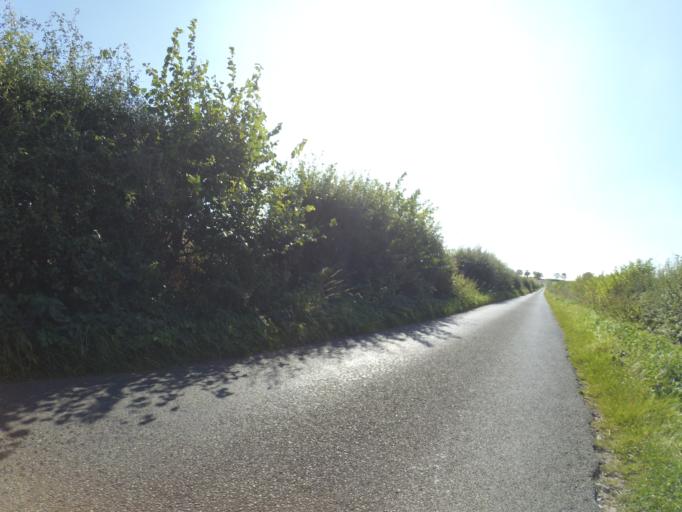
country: GB
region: England
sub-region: Warwickshire
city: Rugby
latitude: 52.4189
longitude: -1.2552
